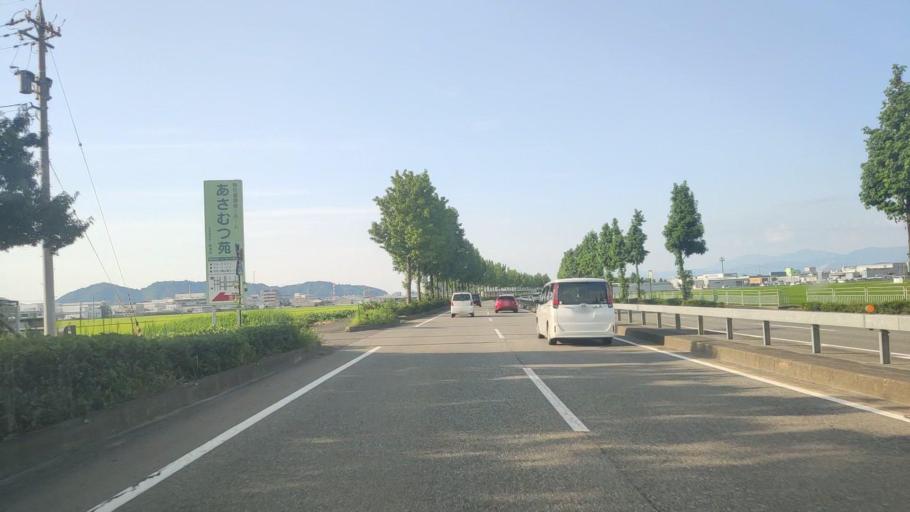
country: JP
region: Fukui
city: Fukui-shi
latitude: 36.0146
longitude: 136.2097
